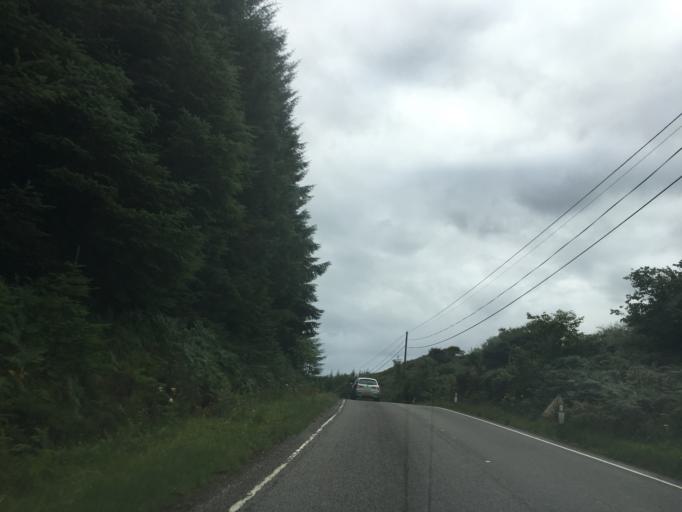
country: GB
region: Scotland
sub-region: Argyll and Bute
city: Oban
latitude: 56.2836
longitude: -5.4810
